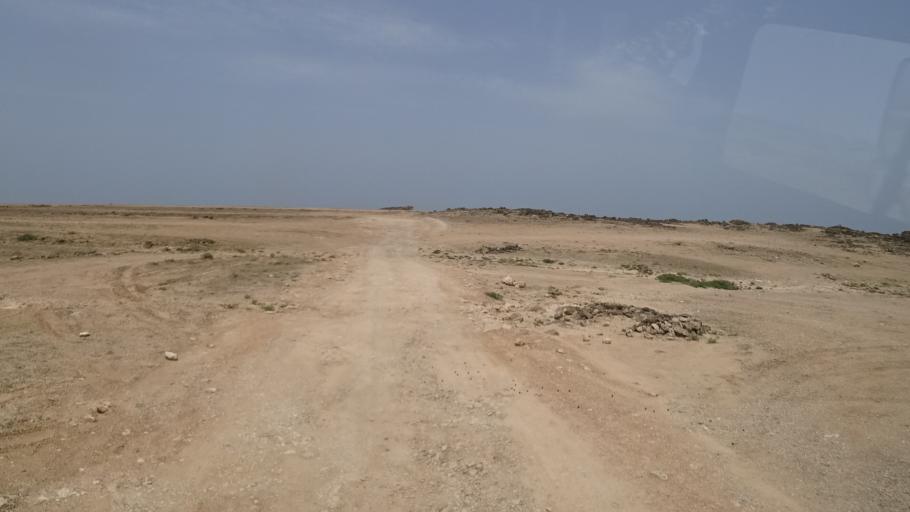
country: OM
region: Zufar
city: Salalah
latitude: 17.0342
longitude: 54.4097
